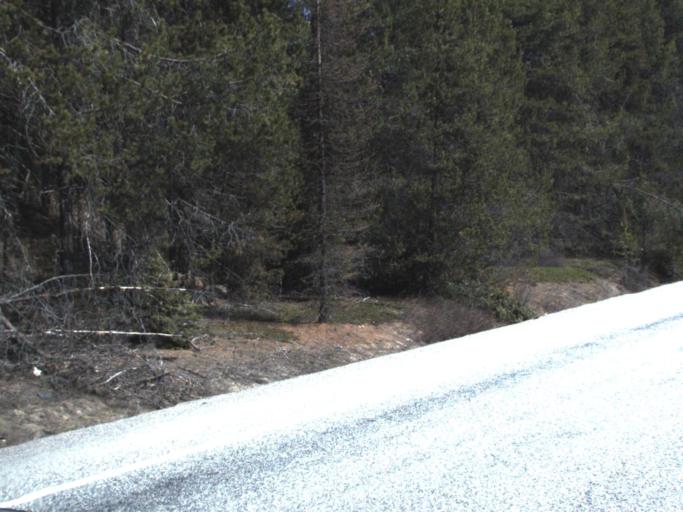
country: US
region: Washington
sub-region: Stevens County
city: Chewelah
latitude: 48.5492
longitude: -117.5699
